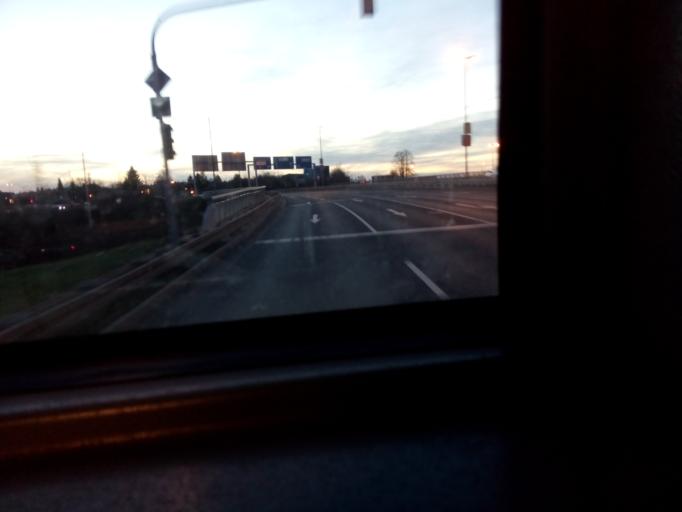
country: CZ
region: Central Bohemia
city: Hostivice
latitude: 50.0944
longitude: 14.2952
